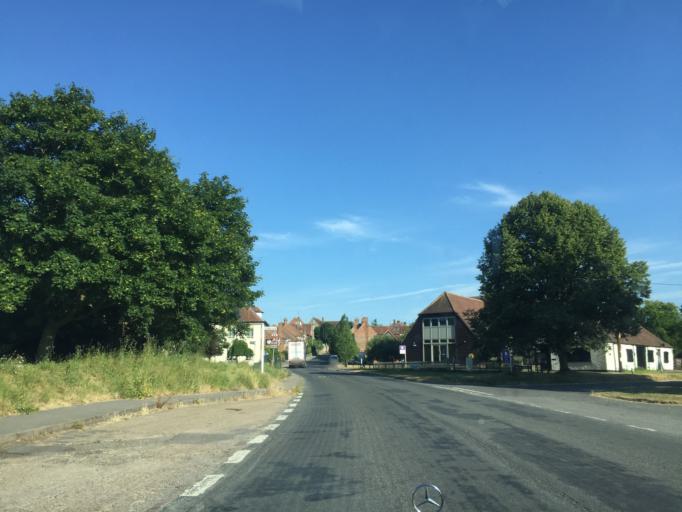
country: GB
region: England
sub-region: Oxfordshire
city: Thame
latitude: 51.7112
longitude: -1.0079
